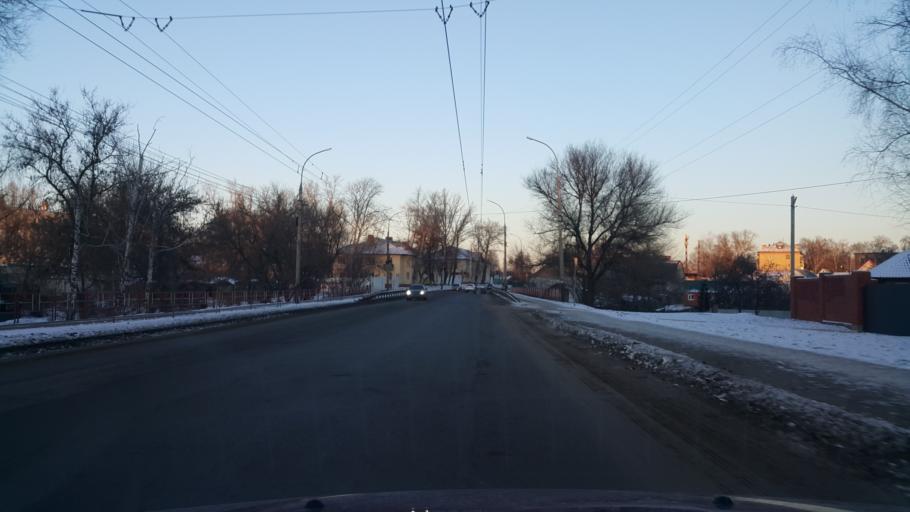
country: RU
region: Tambov
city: Pokrovo-Prigorodnoye
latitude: 52.7116
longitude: 41.3994
